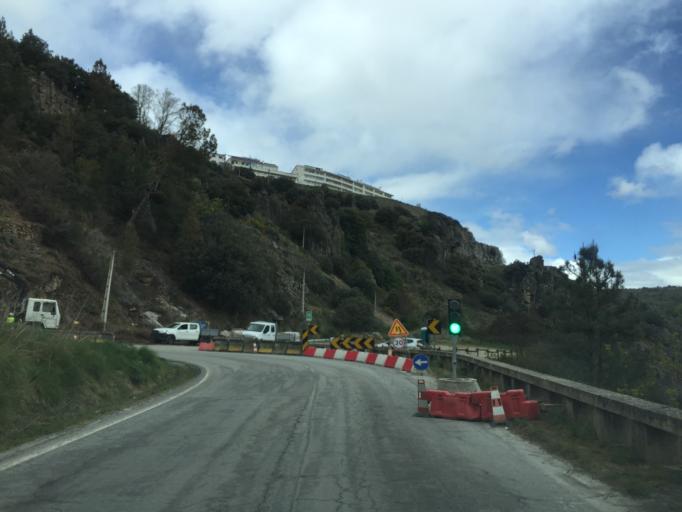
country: PT
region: Braganca
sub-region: Miranda do Douro
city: Miranda do Douro
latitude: 41.4950
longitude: -6.2703
